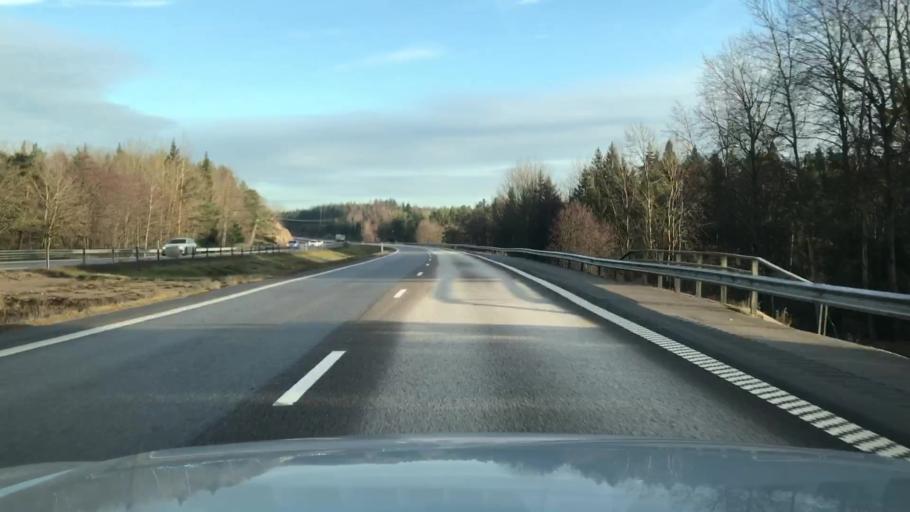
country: SE
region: Soedermanland
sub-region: Nykopings Kommun
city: Nykoping
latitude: 58.8177
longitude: 17.1403
